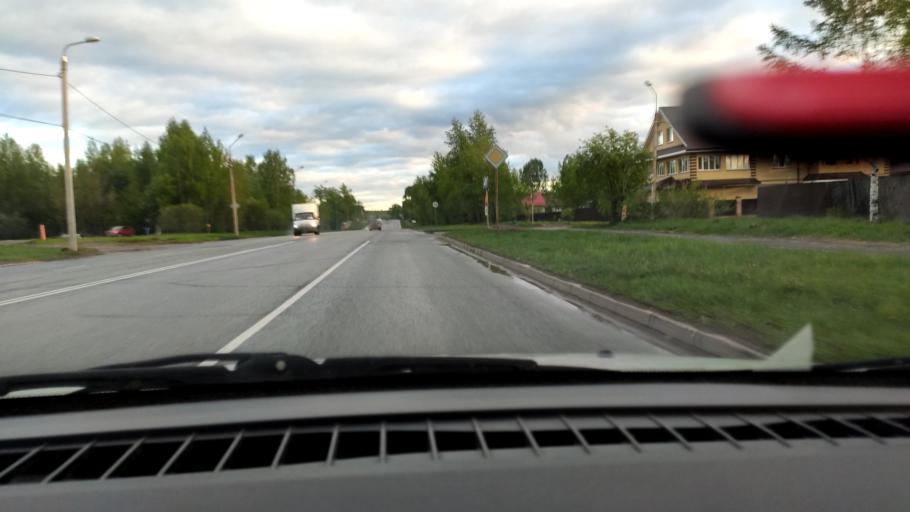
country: RU
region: Perm
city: Polazna
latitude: 58.1274
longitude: 56.4061
